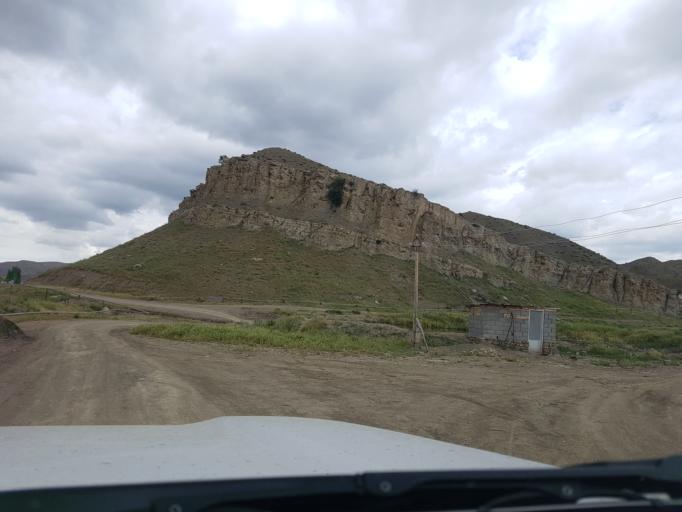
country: TM
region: Ahal
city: Baharly
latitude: 38.2013
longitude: 57.0048
